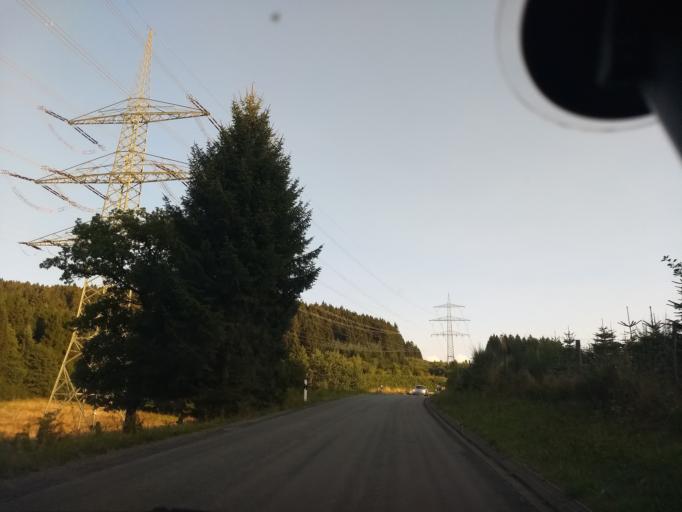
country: DE
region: North Rhine-Westphalia
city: Eslohe
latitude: 51.2622
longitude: 8.0836
